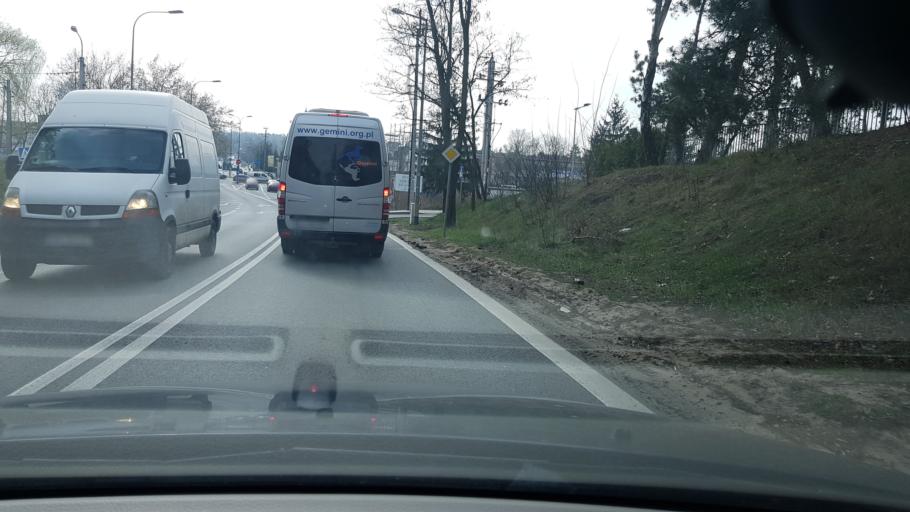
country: PL
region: Masovian Voivodeship
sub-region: Warszawa
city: Wesola
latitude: 52.2252
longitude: 21.2233
